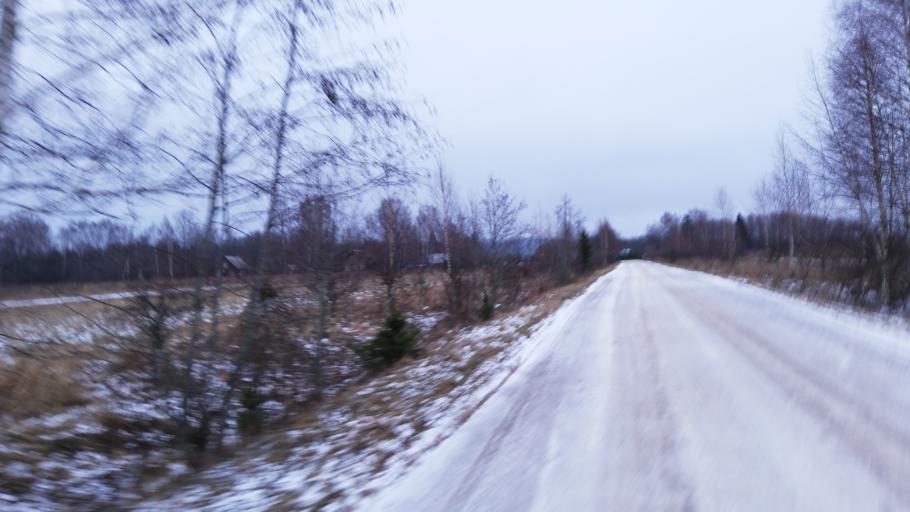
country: RU
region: Kostroma
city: Krasnoye-na-Volge
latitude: 57.6733
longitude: 41.2020
